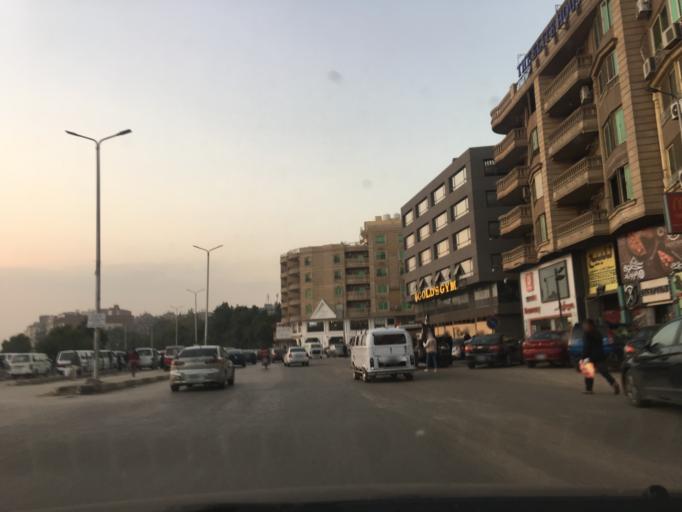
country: EG
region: Al Jizah
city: Al Jizah
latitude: 29.9880
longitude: 31.1406
